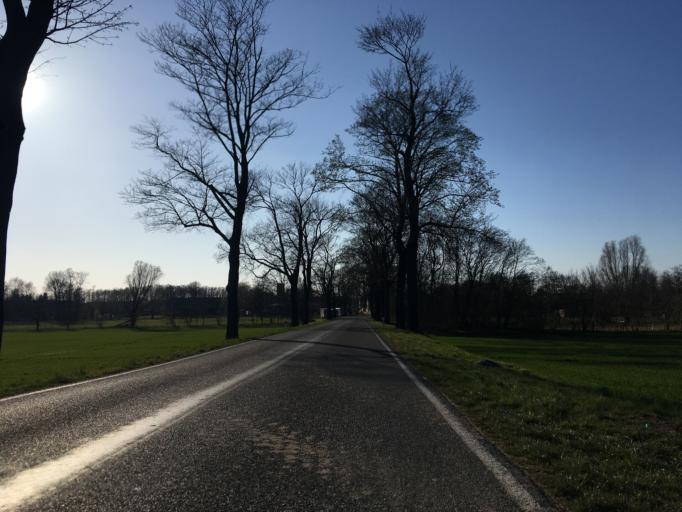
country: DE
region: Berlin
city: Buch
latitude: 52.6244
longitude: 13.5497
